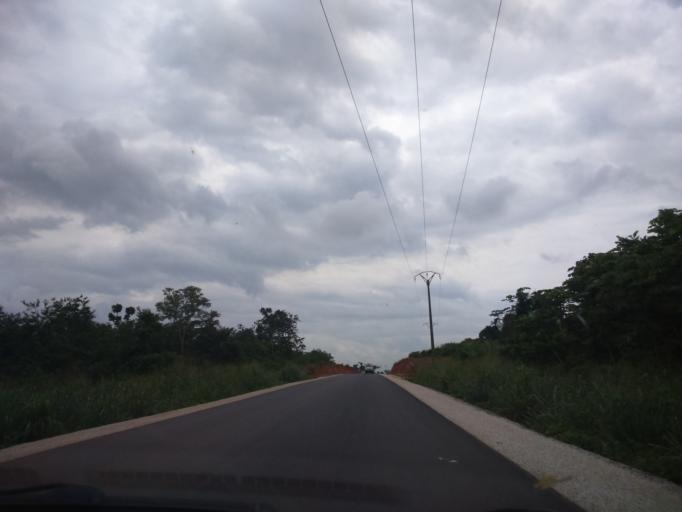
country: CI
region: Lagunes
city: Akoupe
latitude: 6.3302
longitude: -3.8437
